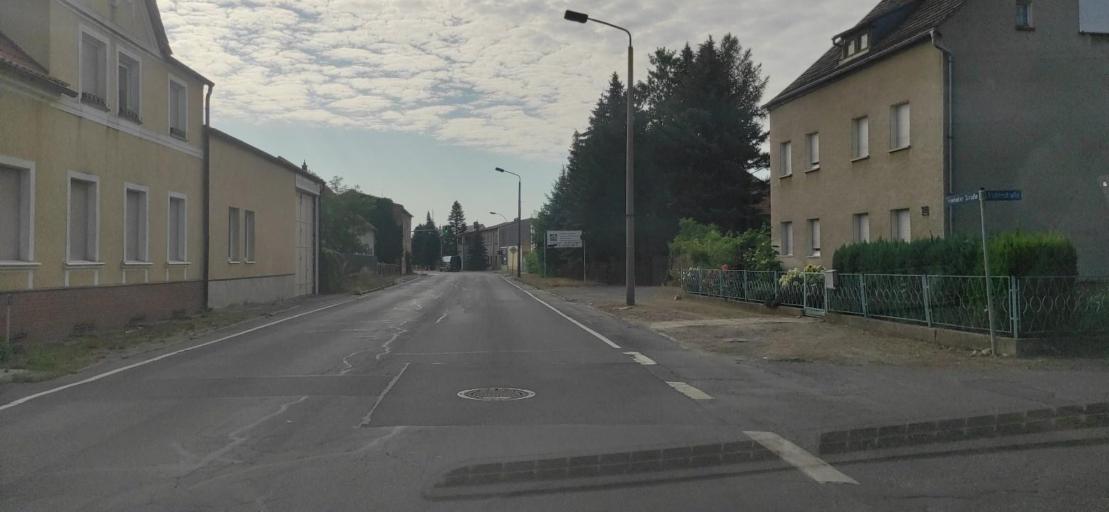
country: DE
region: Brandenburg
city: Forst
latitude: 51.7187
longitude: 14.6604
